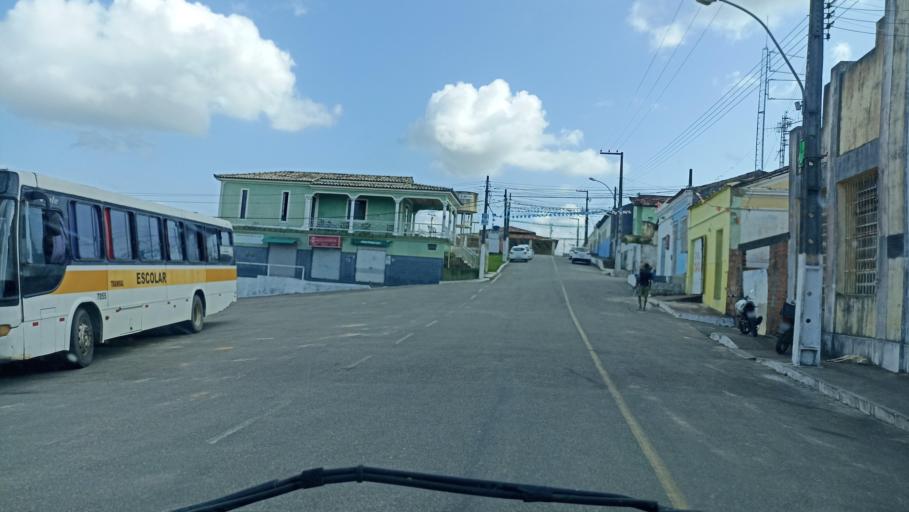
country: BR
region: Sergipe
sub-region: Estancia
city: Estancia
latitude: -11.3527
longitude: -37.4487
